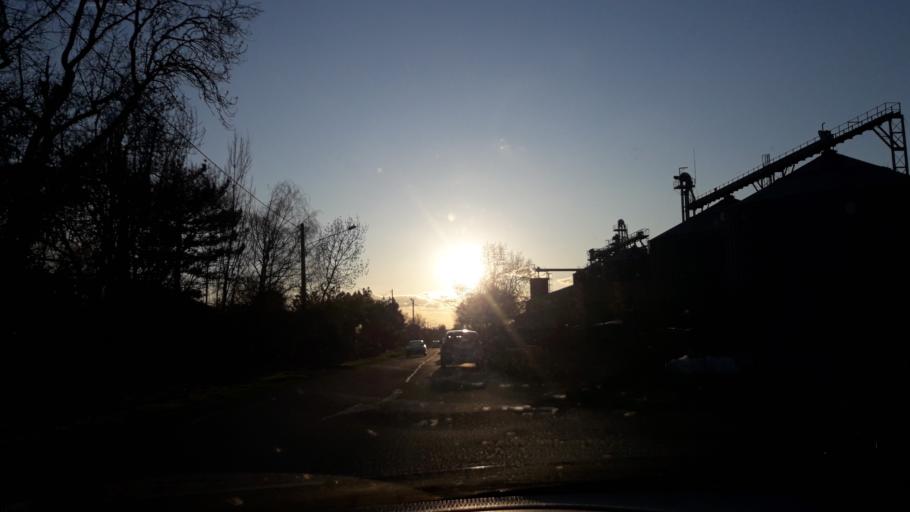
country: FR
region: Midi-Pyrenees
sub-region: Departement du Gers
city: Pujaudran
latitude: 43.6215
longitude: 1.1055
